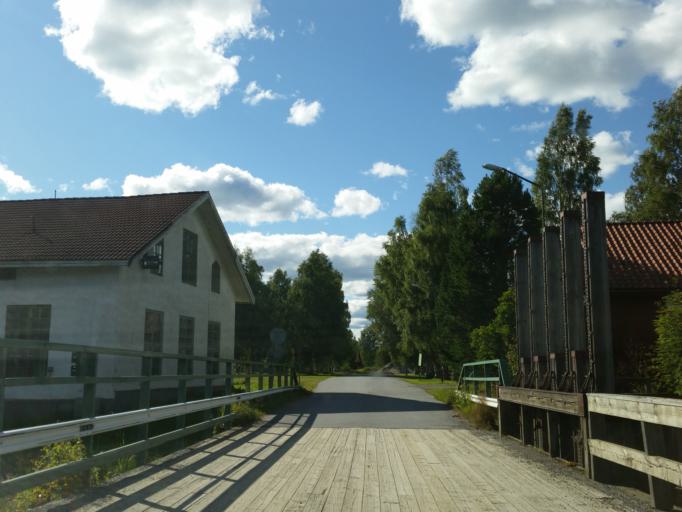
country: SE
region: Vaesterbotten
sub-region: Robertsfors Kommun
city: Robertsfors
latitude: 64.1854
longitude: 20.8489
